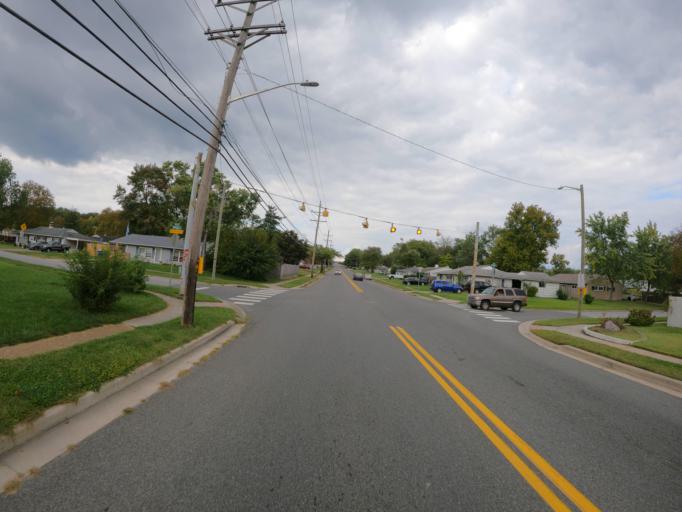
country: US
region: Delaware
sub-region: New Castle County
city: Brookside
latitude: 39.6707
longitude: -75.7277
